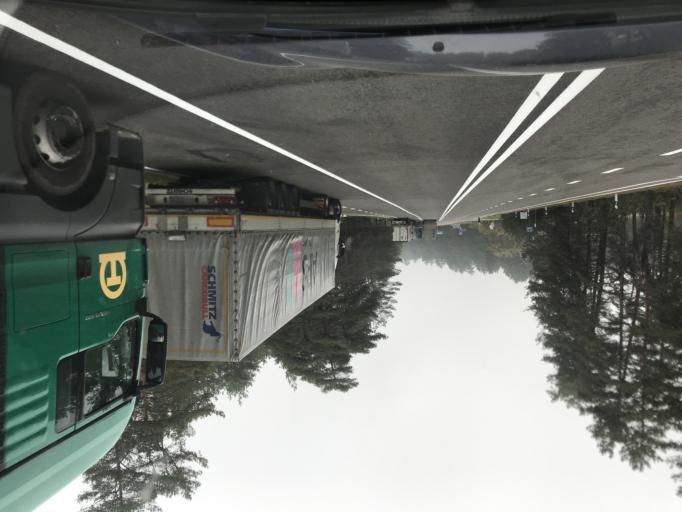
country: LT
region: Alytaus apskritis
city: Druskininkai
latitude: 53.9287
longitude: 23.9368
